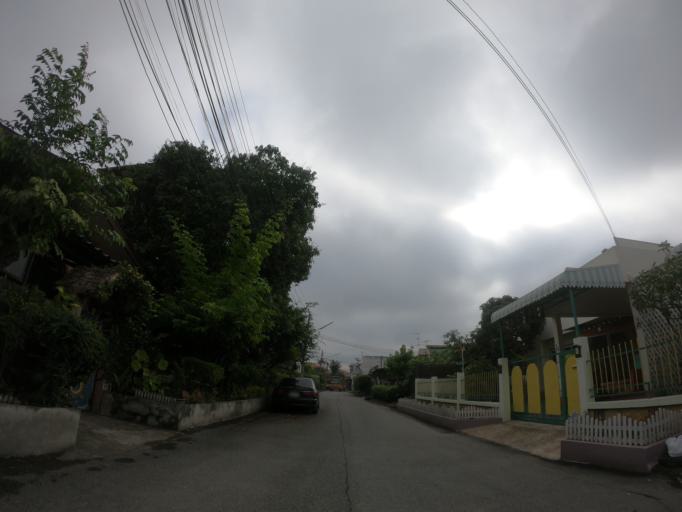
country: TH
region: Chiang Mai
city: Chiang Mai
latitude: 18.7620
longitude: 98.9749
